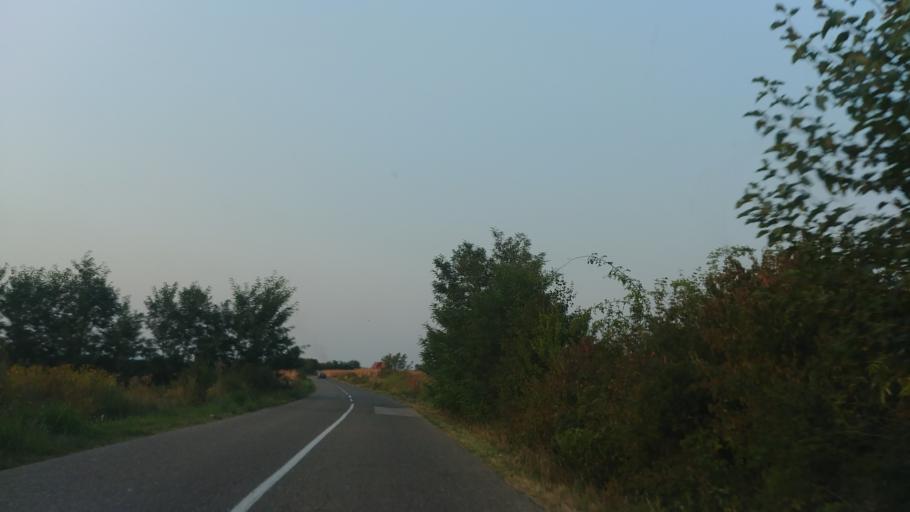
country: BA
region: Republika Srpska
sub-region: Opstina Ugljevik
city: Ugljevik
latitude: 44.7105
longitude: 18.9887
